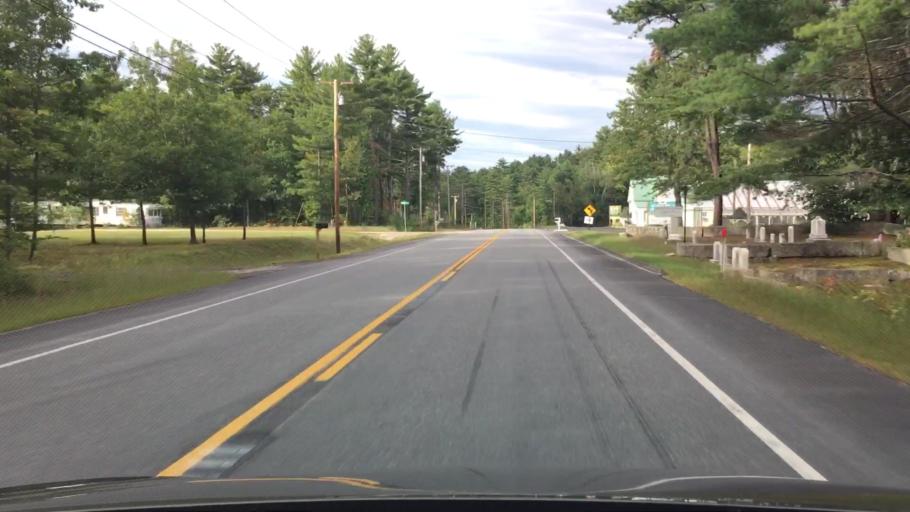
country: US
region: Maine
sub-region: Oxford County
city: Lovell
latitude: 44.0533
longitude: -70.8574
